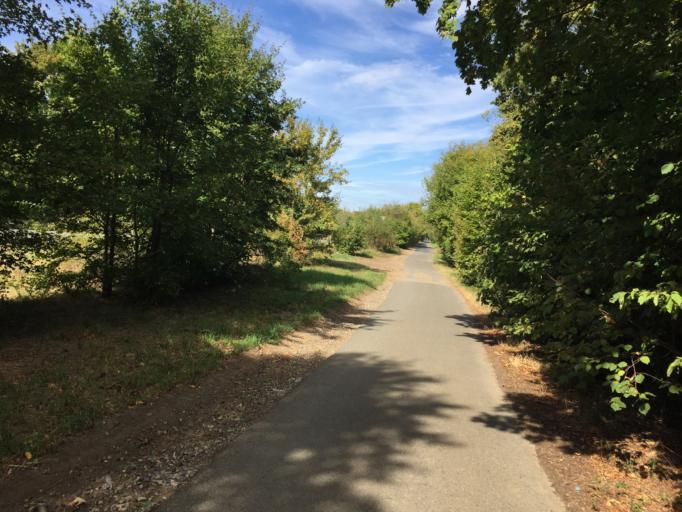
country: DE
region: Hesse
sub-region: Regierungsbezirk Giessen
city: Langgons
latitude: 50.4834
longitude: 8.6573
